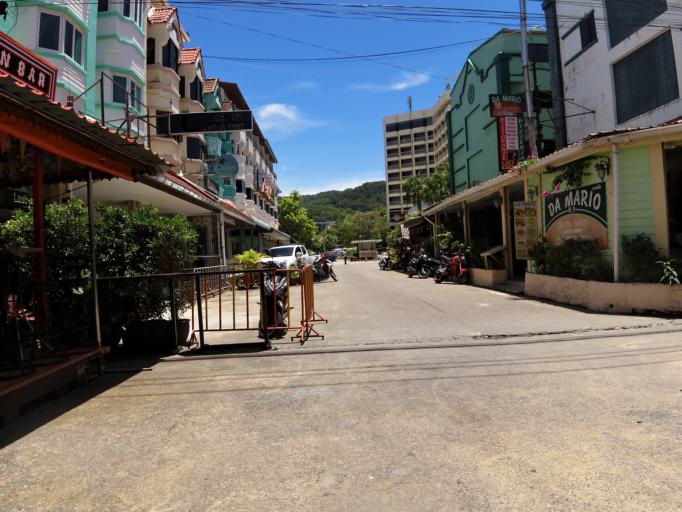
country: TH
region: Phuket
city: Ban Karon
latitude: 7.8498
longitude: 98.2955
